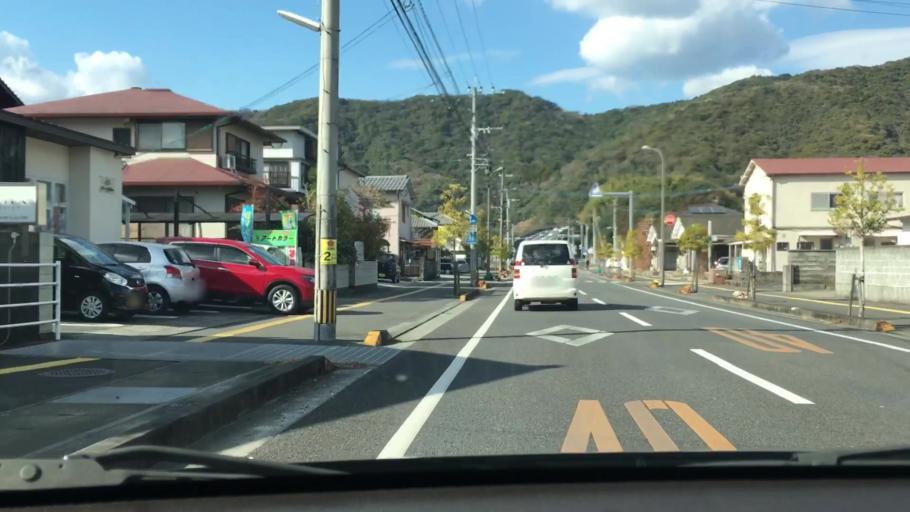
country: JP
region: Oita
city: Saiki
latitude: 32.9629
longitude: 131.8977
